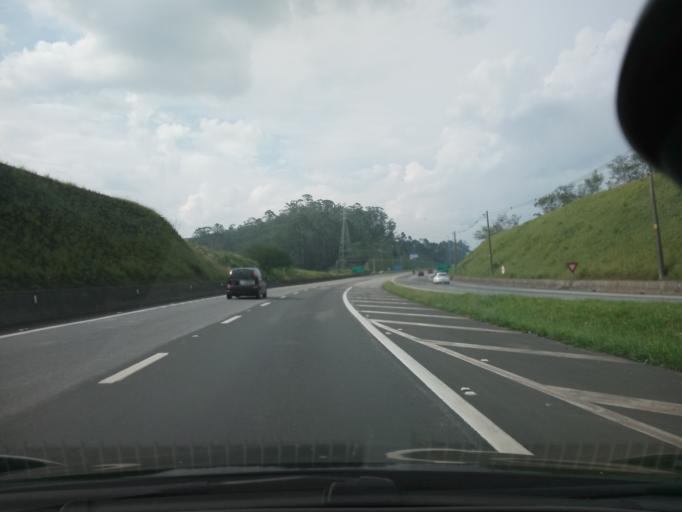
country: BR
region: Sao Paulo
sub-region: Sao Bernardo Do Campo
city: Sao Bernardo do Campo
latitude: -23.7600
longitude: -46.5458
